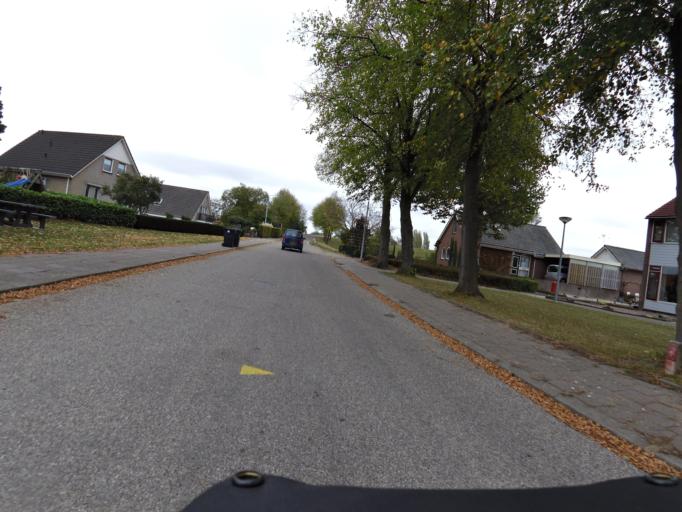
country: NL
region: Gelderland
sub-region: Gemeente Zevenaar
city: Zevenaar
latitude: 51.8878
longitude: 6.0447
